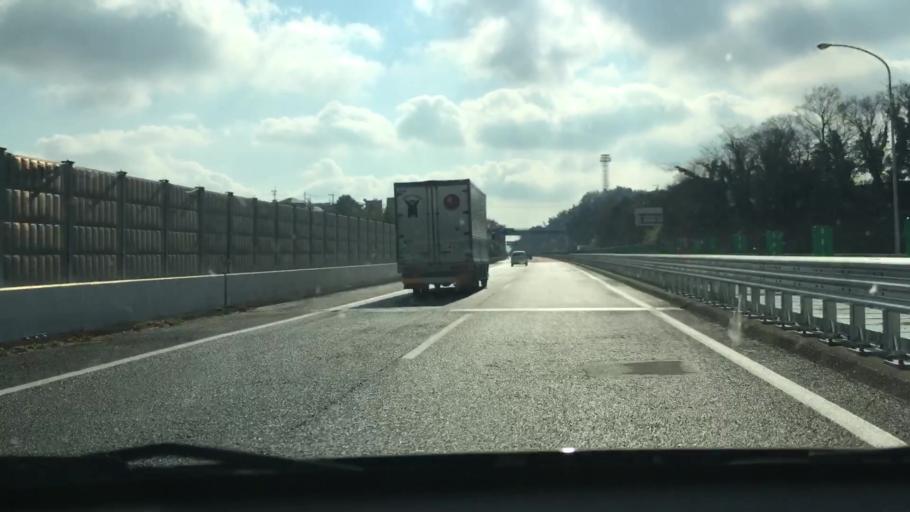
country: JP
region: Kumamoto
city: Kumamoto
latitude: 32.7309
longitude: 130.7752
